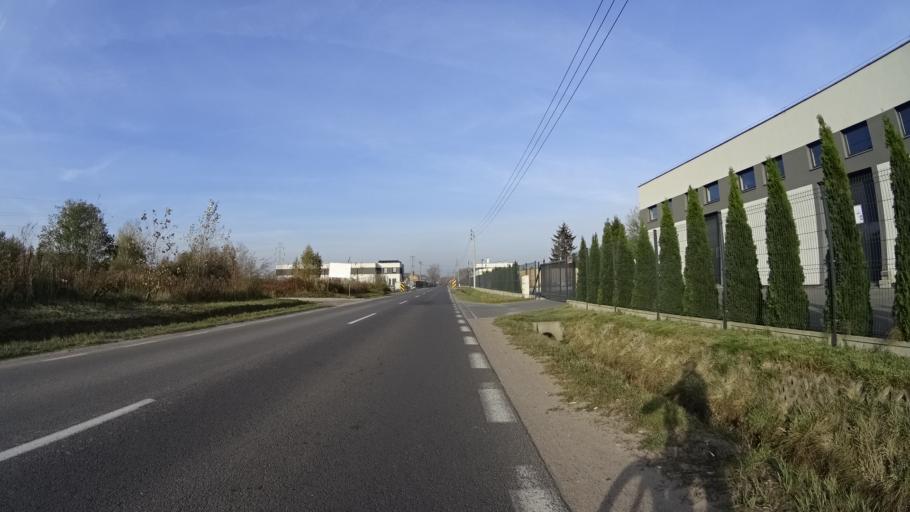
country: PL
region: Masovian Voivodeship
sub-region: Powiat warszawski zachodni
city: Babice
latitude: 52.2789
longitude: 20.8665
